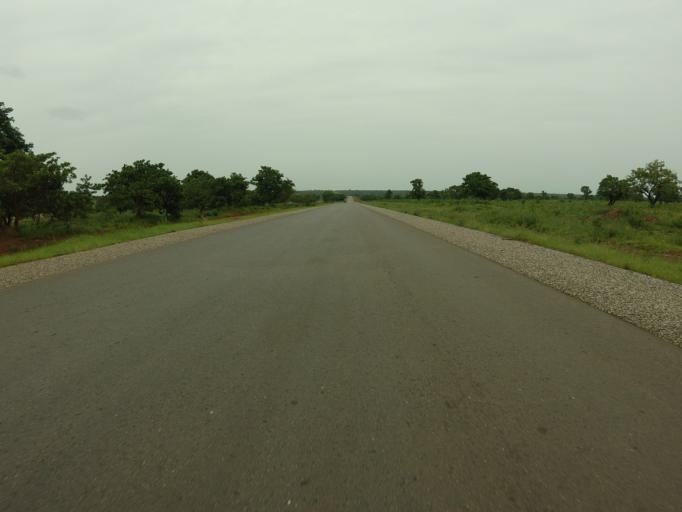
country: GH
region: Northern
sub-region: Yendi
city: Yendi
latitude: 9.2701
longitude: 0.0181
